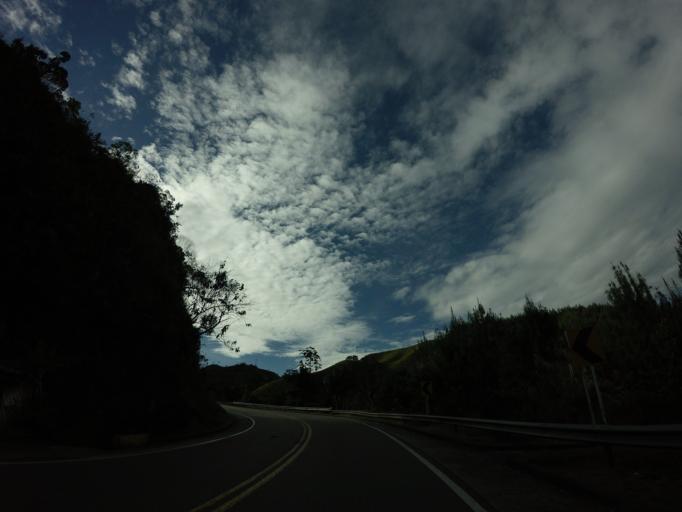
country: CO
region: Tolima
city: Casabianca
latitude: 5.1373
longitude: -75.1347
